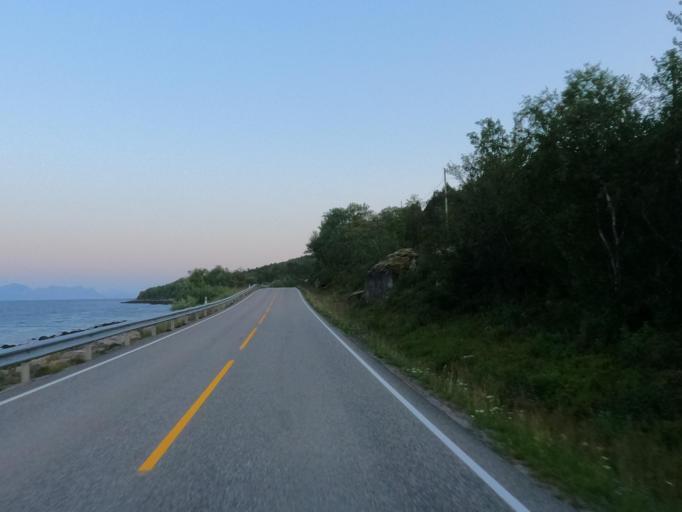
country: NO
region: Nordland
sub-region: Lodingen
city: Lodingen
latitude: 68.4827
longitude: 16.0881
